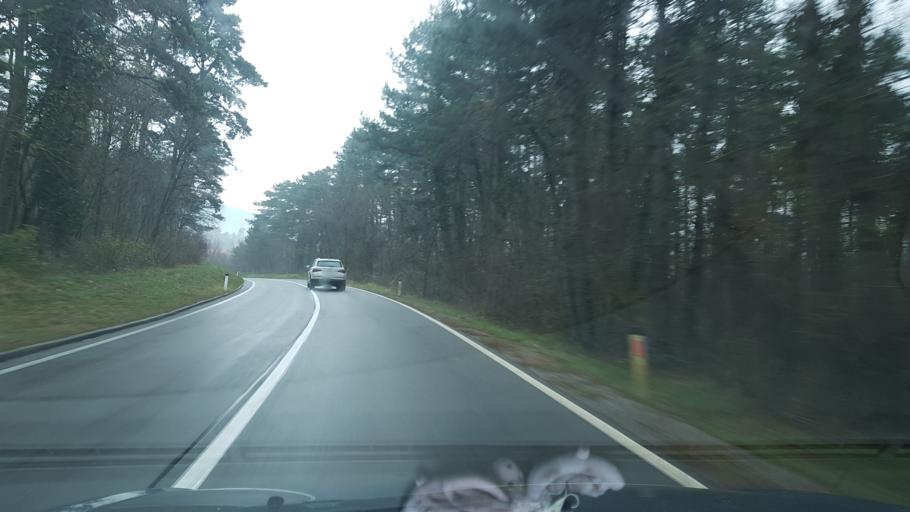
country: SI
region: Sezana
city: Sezana
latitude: 45.7300
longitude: 13.8673
